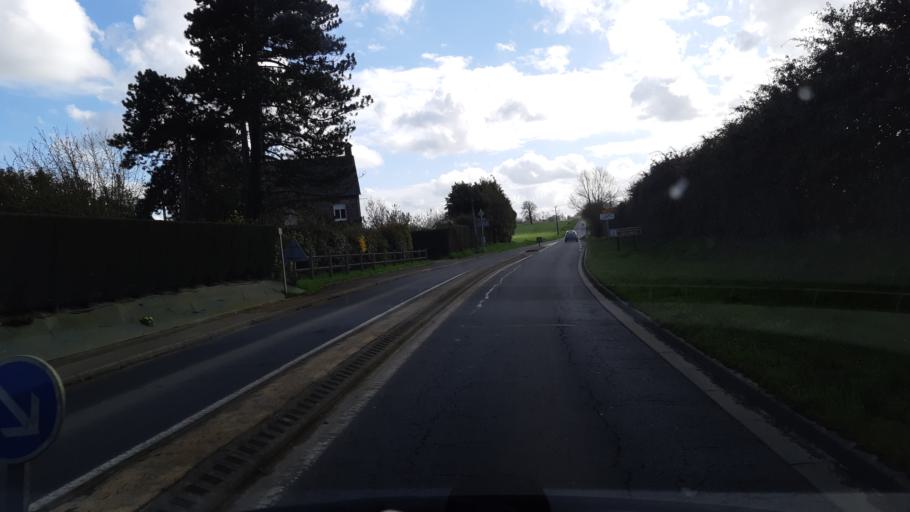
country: FR
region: Lower Normandy
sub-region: Departement de la Manche
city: Agneaux
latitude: 49.0453
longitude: -1.1281
